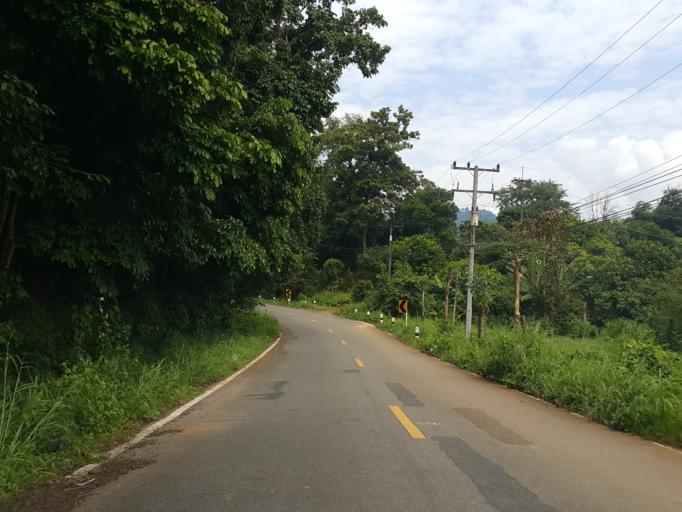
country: TH
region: Mae Hong Son
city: Mae Hong Son
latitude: 19.4753
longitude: 97.9662
